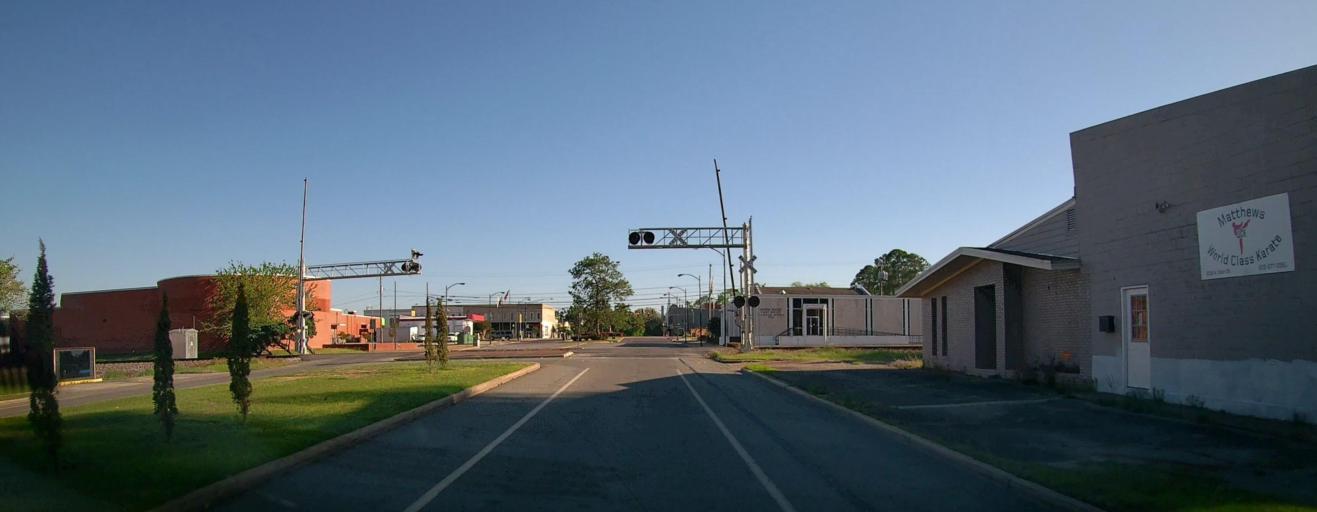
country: US
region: Georgia
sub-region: Ben Hill County
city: Fitzgerald
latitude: 31.7166
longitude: -83.2546
